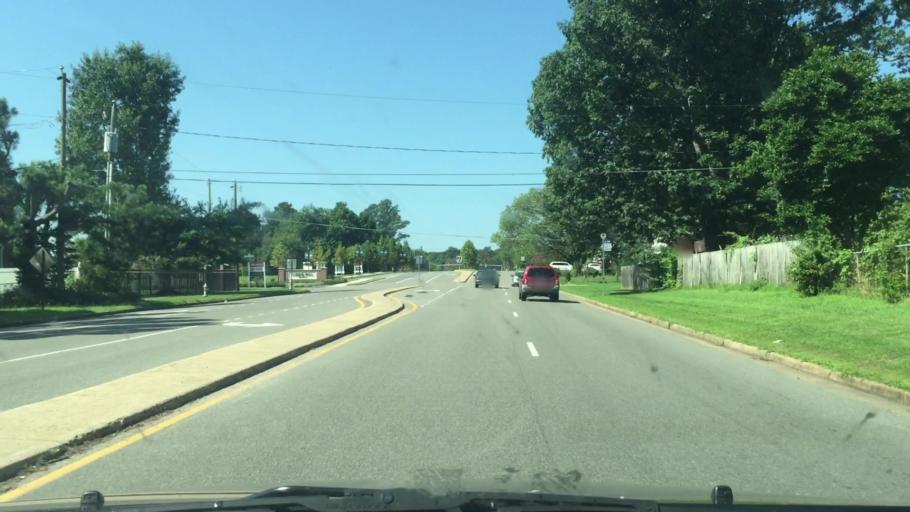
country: US
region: Virginia
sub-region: Henrico County
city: Dumbarton
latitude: 37.5924
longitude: -77.5011
